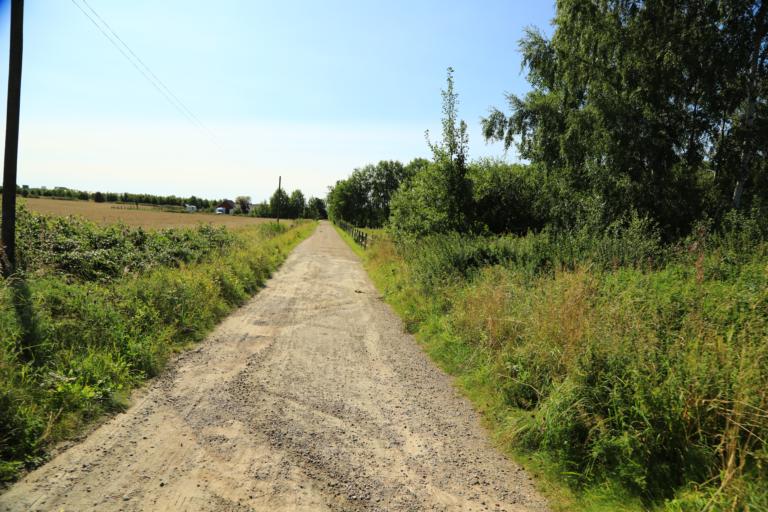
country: SE
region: Halland
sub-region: Varbergs Kommun
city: Traslovslage
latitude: 57.0913
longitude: 12.2834
